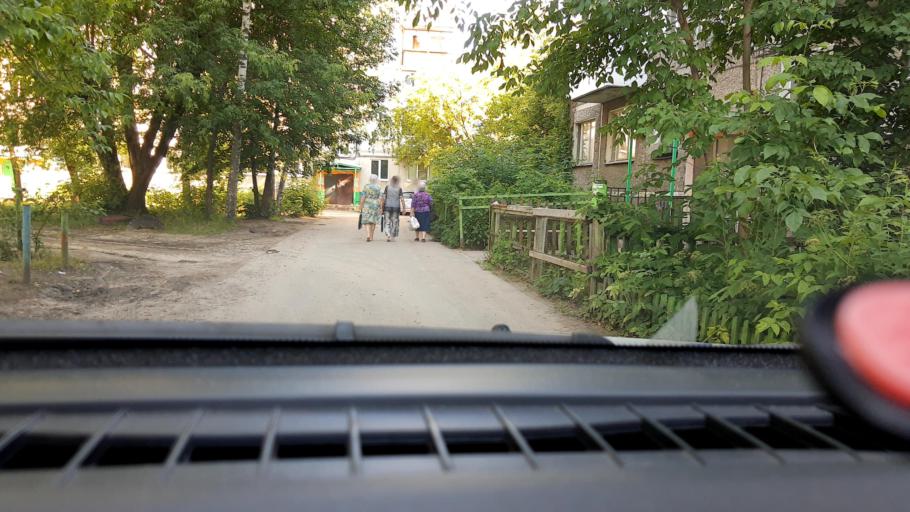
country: RU
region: Nizjnij Novgorod
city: Dzerzhinsk
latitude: 56.2271
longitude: 43.4229
